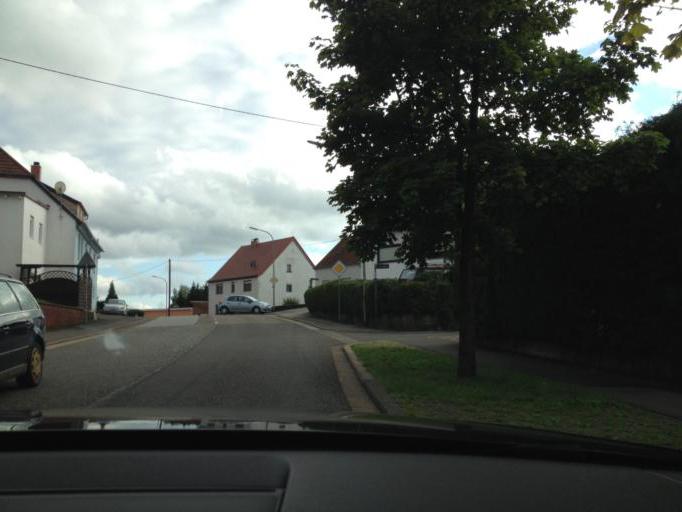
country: DE
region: Saarland
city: Namborn
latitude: 49.5122
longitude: 7.1570
